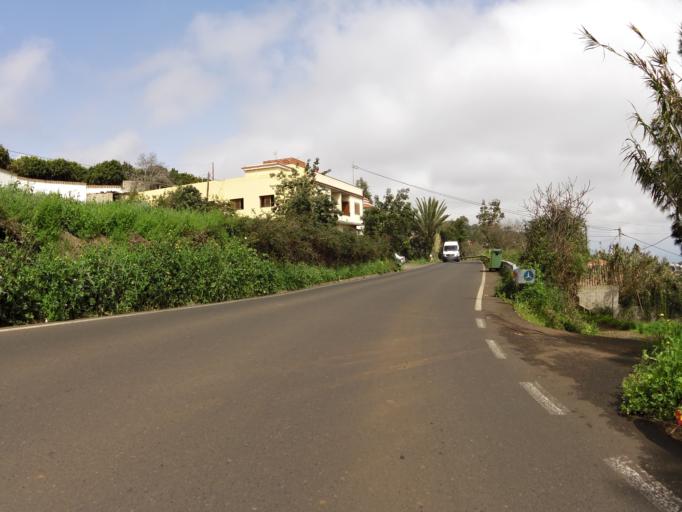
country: ES
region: Canary Islands
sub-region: Provincia de Las Palmas
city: Teror
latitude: 28.0806
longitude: -15.5425
